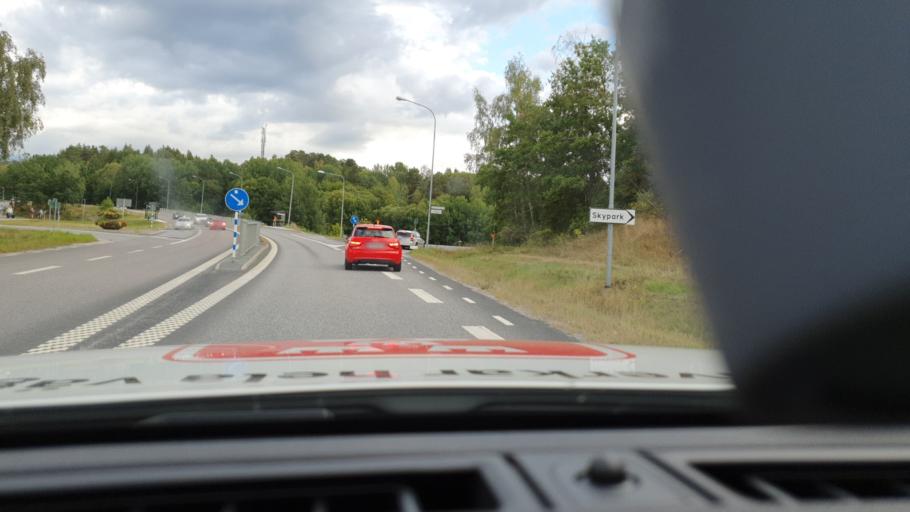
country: SE
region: Stockholm
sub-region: Vaxholms Kommun
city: Resaro
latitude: 59.4068
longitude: 18.3173
